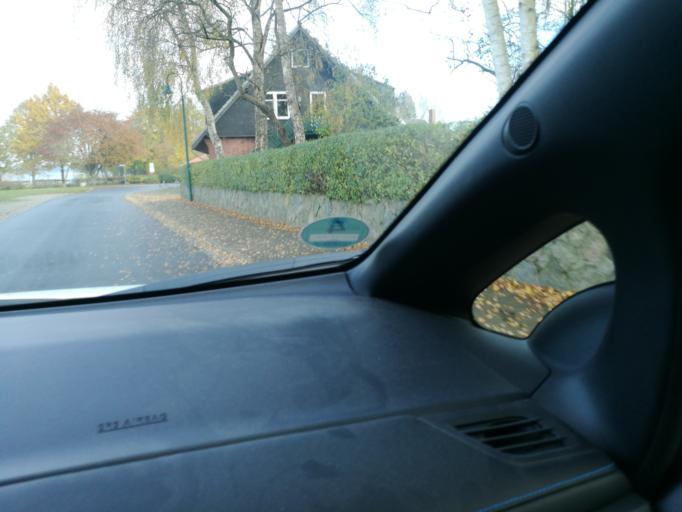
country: DE
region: Schleswig-Holstein
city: Bunsdorf
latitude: 54.3698
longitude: 9.7428
